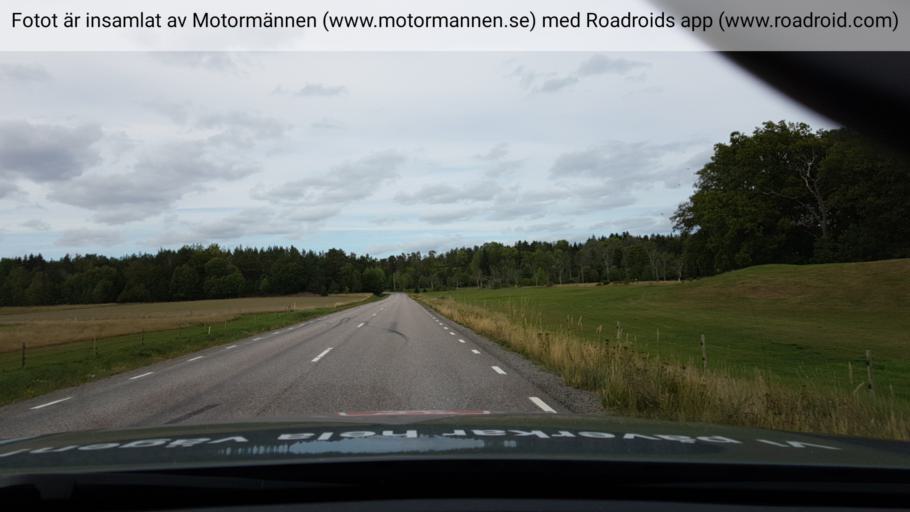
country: SE
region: Stockholm
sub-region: Haninge Kommun
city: Haninge
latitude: 59.1114
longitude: 18.1890
